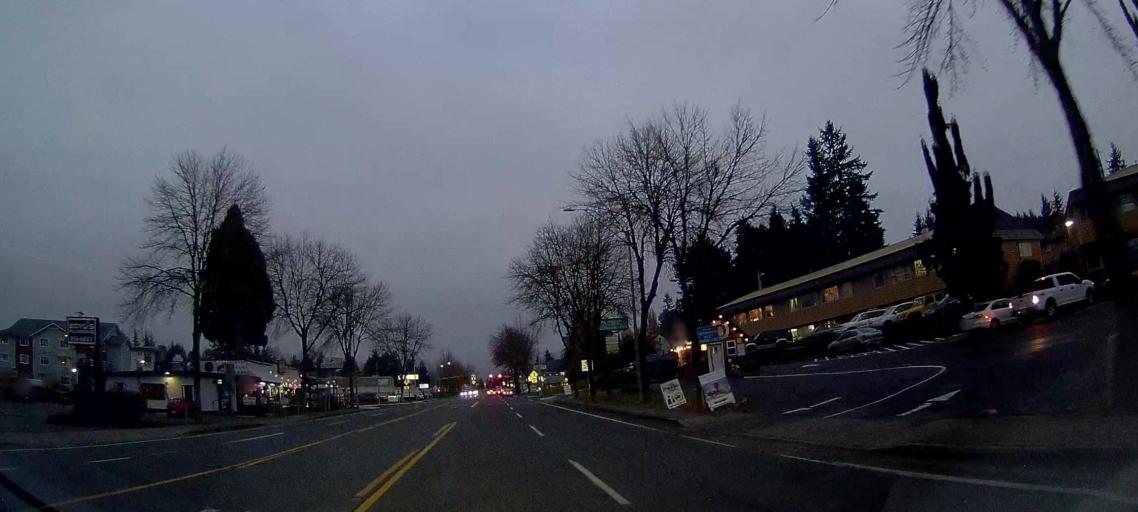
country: US
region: Washington
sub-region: Thurston County
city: Olympia
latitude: 47.0434
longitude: -122.8618
